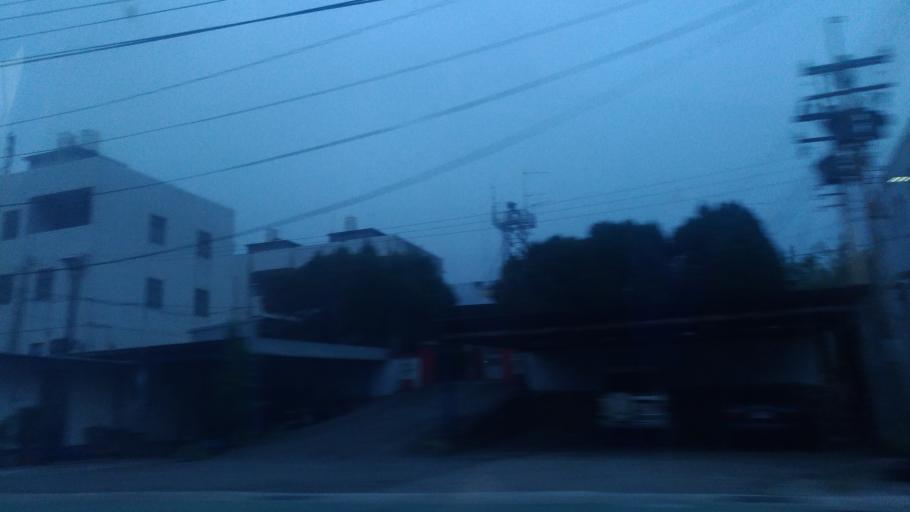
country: TW
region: Taiwan
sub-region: Miaoli
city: Miaoli
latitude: 24.5645
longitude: 120.7103
